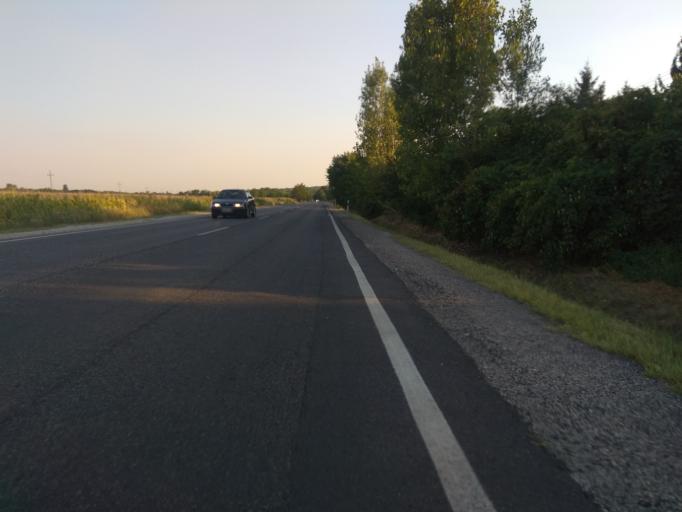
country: HU
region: Borsod-Abauj-Zemplen
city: Nyekladhaza
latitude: 47.9809
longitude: 20.8308
